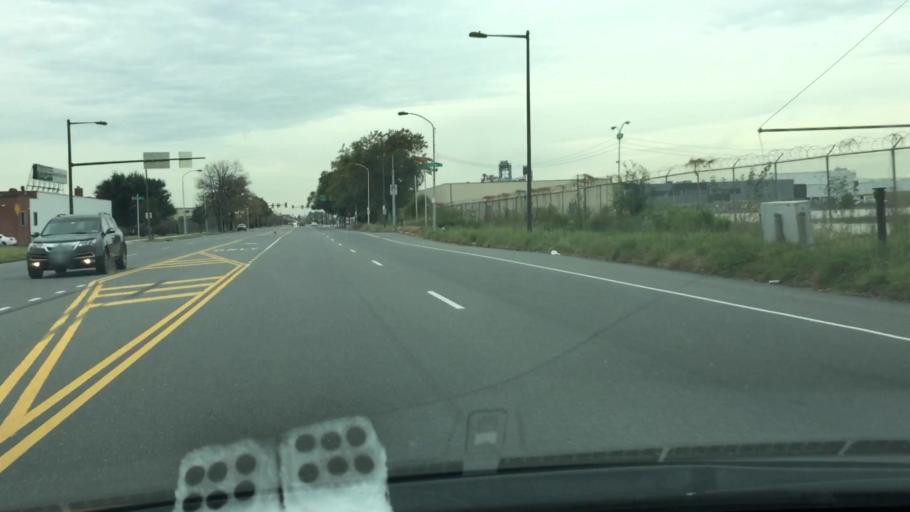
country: US
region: New Jersey
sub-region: Camden County
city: Gloucester City
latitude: 39.9031
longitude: -75.1554
